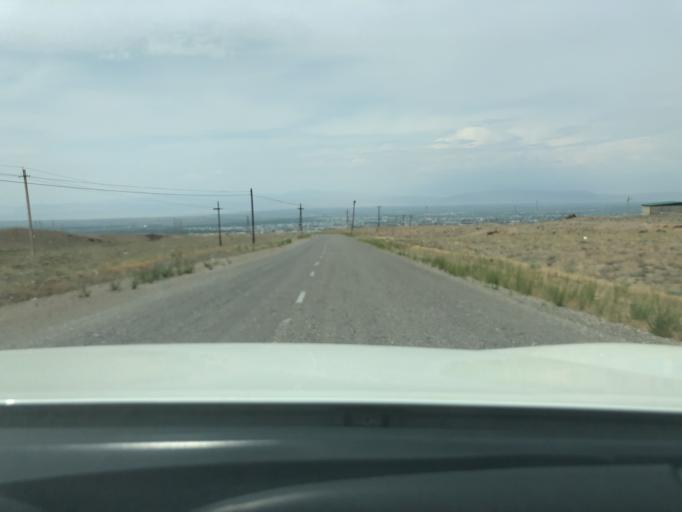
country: TJ
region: Viloyati Sughd
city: Kim
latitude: 40.2506
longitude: 70.4662
